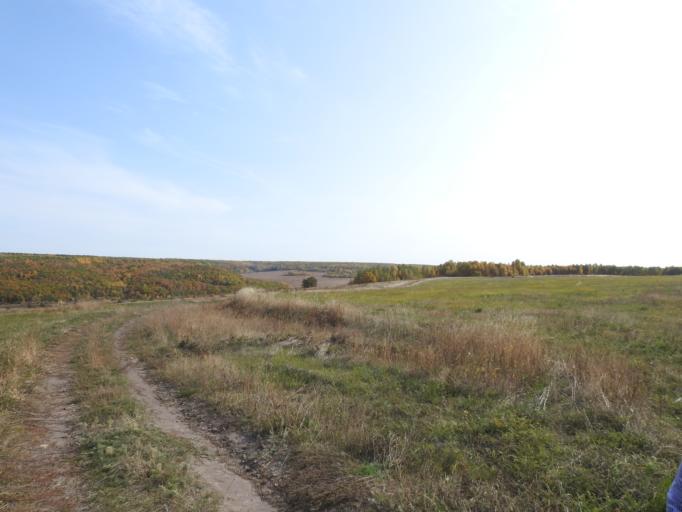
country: RU
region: Saratov
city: Baltay
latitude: 52.5218
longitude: 46.6730
